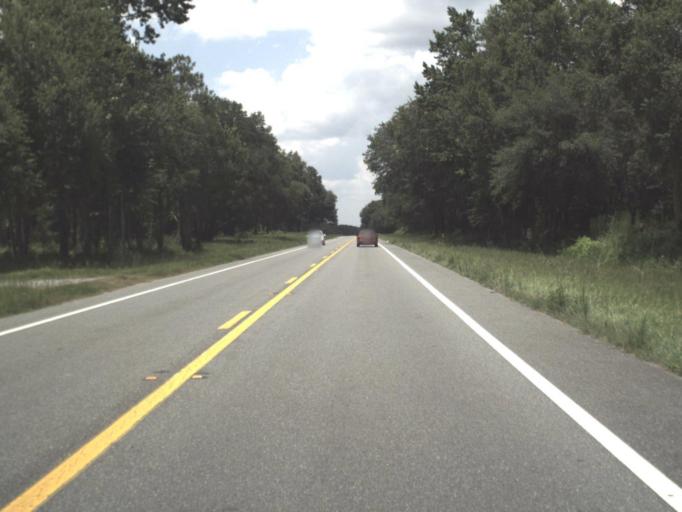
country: US
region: Florida
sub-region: Columbia County
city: Five Points
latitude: 30.2899
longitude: -82.7046
